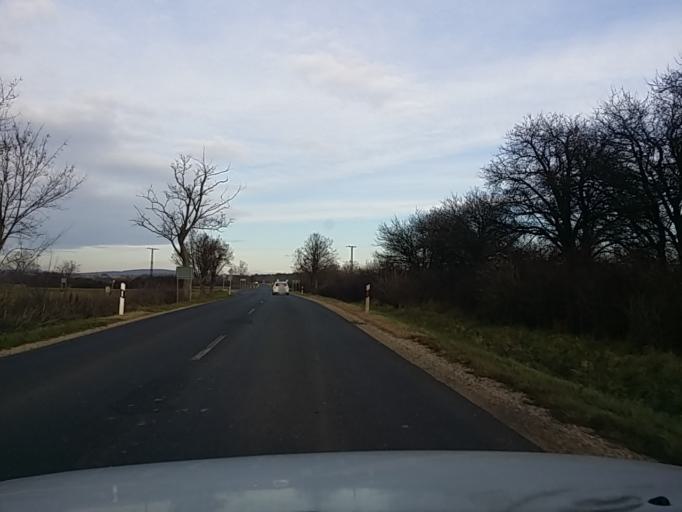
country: HU
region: Veszprem
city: Urkut
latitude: 46.9954
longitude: 17.7303
